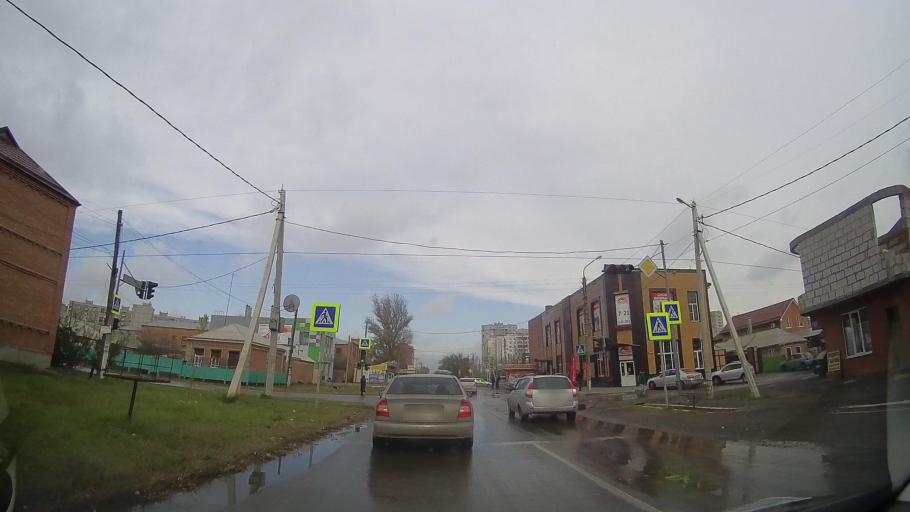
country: RU
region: Rostov
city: Bataysk
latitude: 47.1332
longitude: 39.7677
